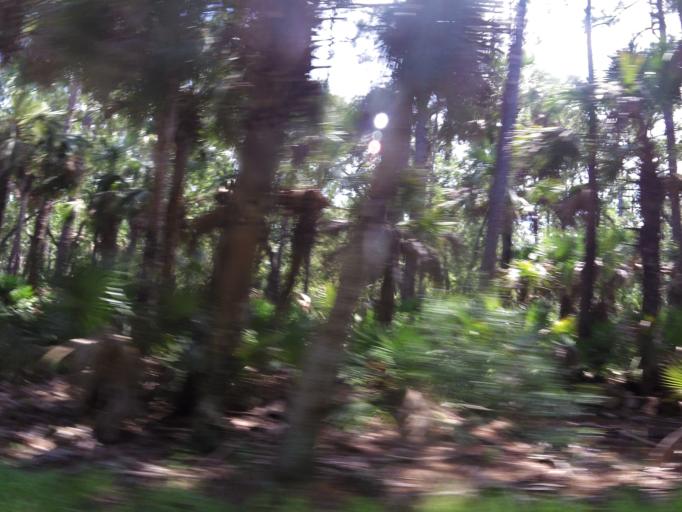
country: US
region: Florida
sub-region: Volusia County
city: Ormond-by-the-Sea
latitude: 29.3552
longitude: -81.1086
